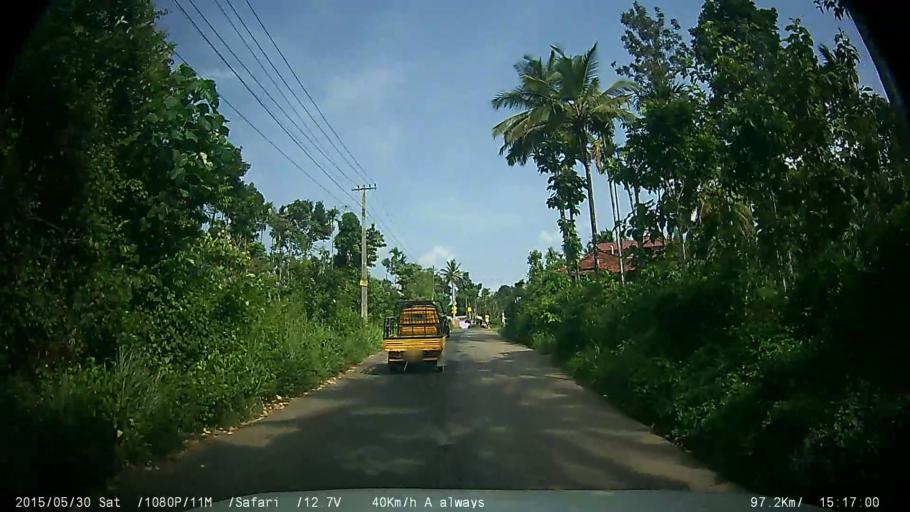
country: IN
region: Kerala
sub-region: Wayanad
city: Panamaram
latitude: 11.7747
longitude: 76.0590
